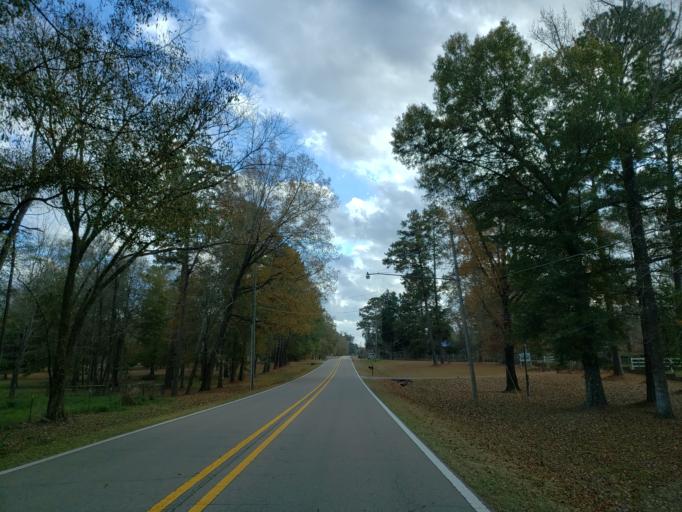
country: US
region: Mississippi
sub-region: Forrest County
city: Hattiesburg
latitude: 31.2682
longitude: -89.2928
